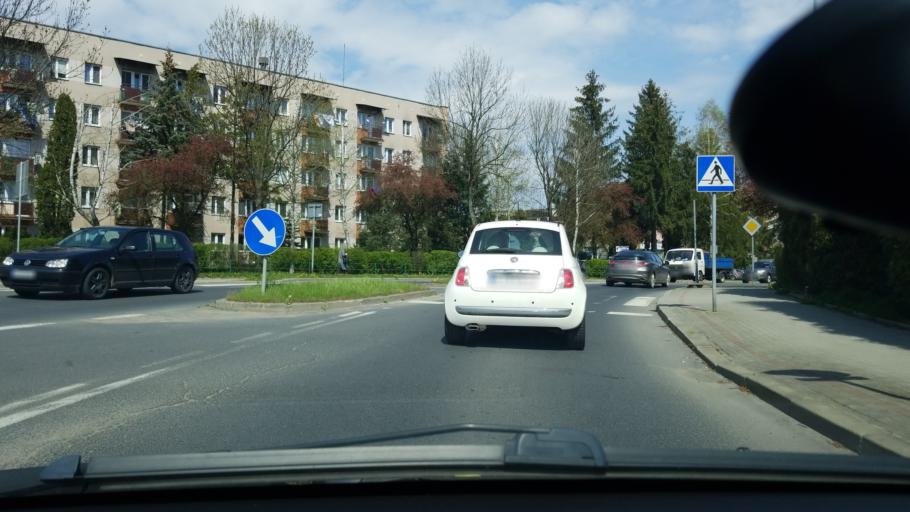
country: PL
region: Subcarpathian Voivodeship
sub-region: Powiat jasielski
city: Jaslo
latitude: 49.7369
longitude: 21.4665
